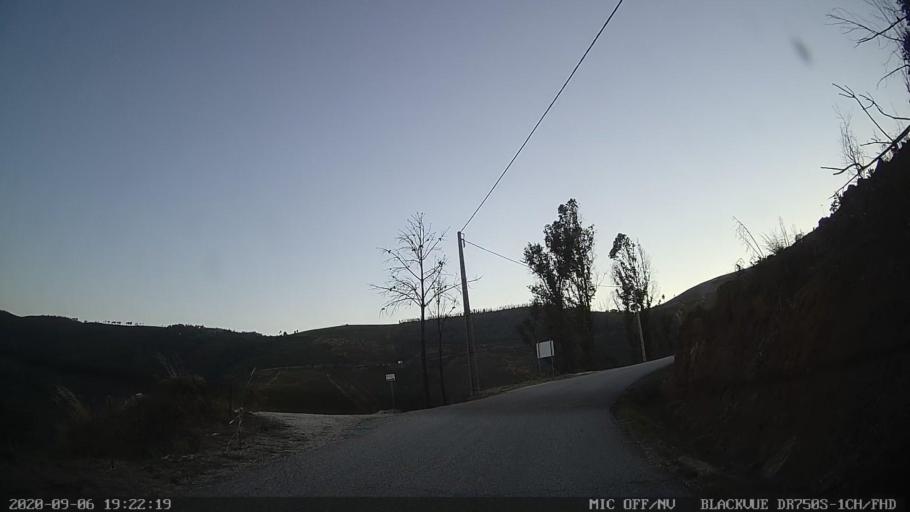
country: PT
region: Vila Real
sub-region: Mesao Frio
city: Mesao Frio
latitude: 41.1833
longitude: -7.9263
